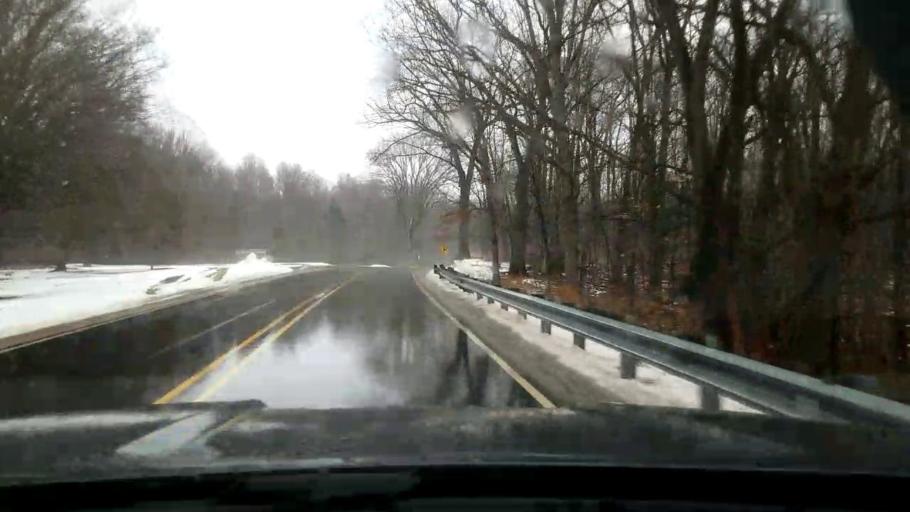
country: US
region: Michigan
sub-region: Jackson County
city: Grass Lake
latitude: 42.3248
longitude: -84.2427
